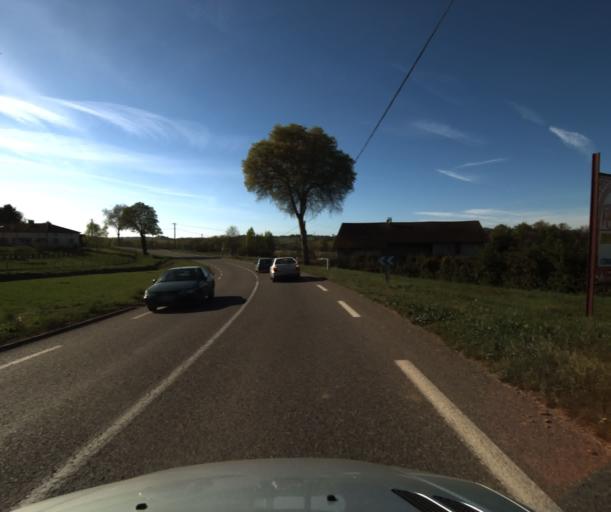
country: FR
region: Midi-Pyrenees
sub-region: Departement du Tarn-et-Garonne
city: Lafrancaise
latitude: 44.1362
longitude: 1.2192
